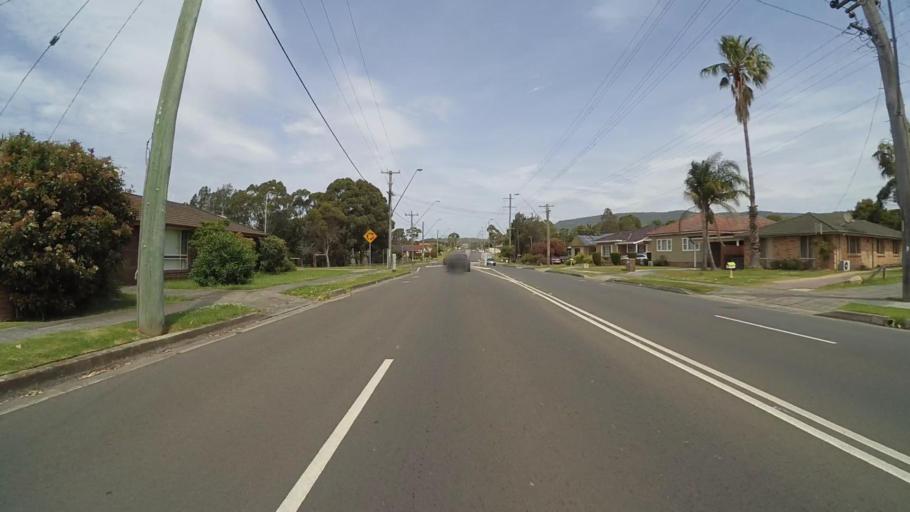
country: AU
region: New South Wales
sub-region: Shellharbour
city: Albion Park Rail
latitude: -34.5747
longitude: 150.7762
